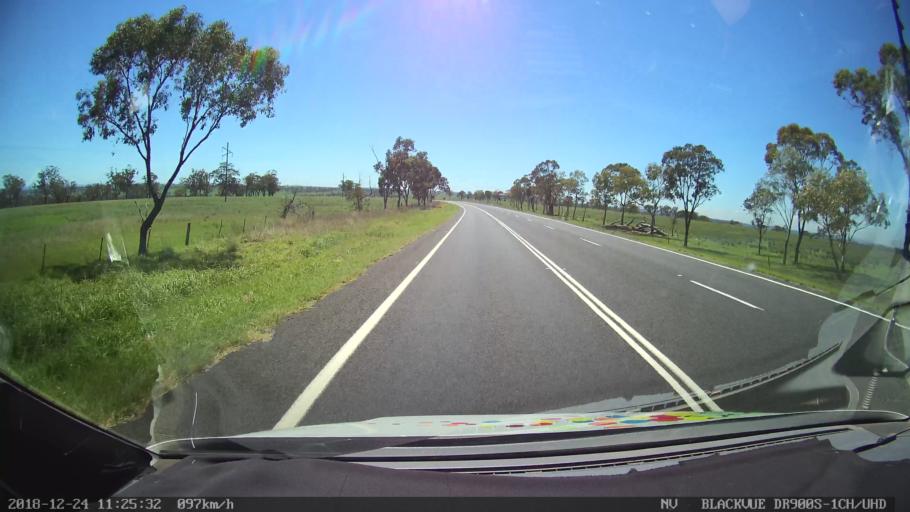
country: AU
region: New South Wales
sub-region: Upper Hunter Shire
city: Merriwa
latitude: -32.1698
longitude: 150.4177
